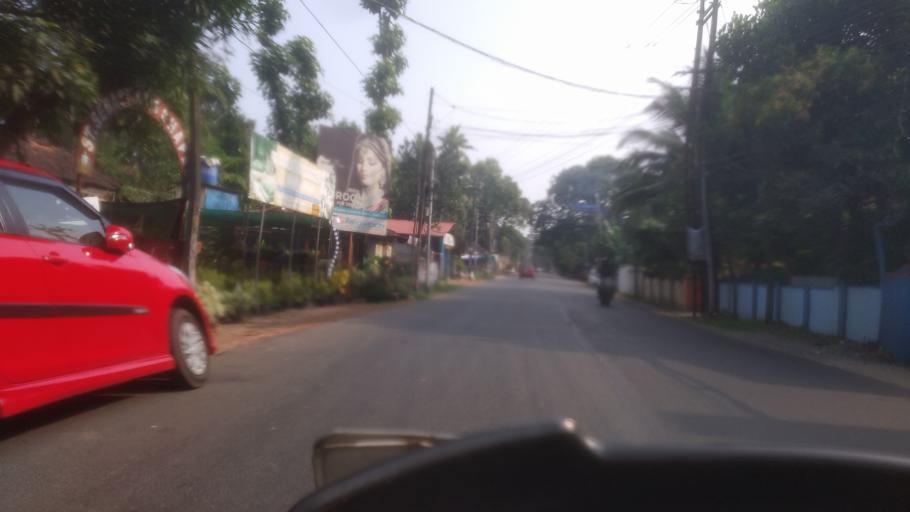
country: IN
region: Kerala
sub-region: Alappuzha
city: Arukutti
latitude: 9.9373
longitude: 76.3522
